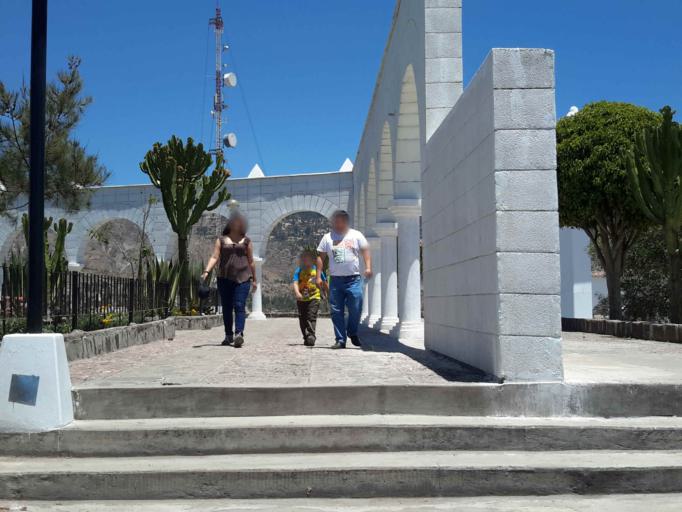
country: PE
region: Ayacucho
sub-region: Provincia de Huamanga
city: Carmen Alto
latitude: -13.1716
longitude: -74.2218
